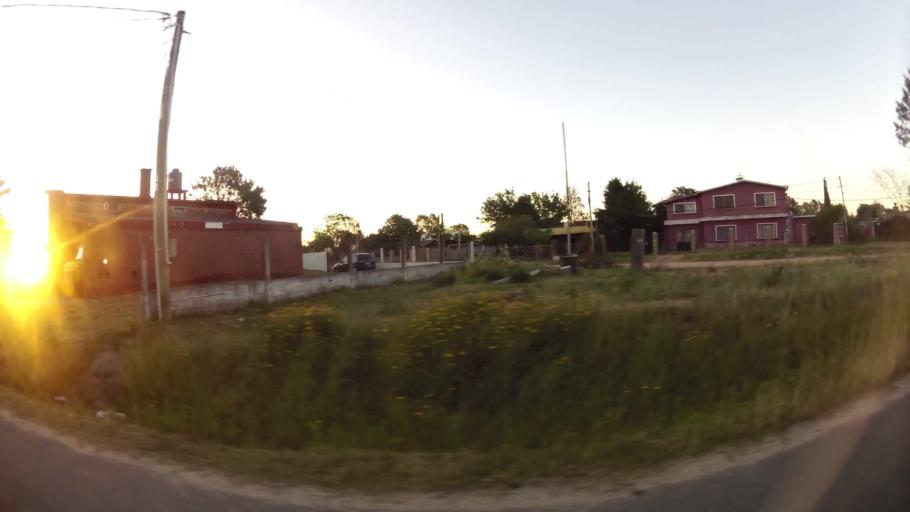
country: UY
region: Canelones
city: Barra de Carrasco
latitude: -34.8317
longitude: -55.9623
